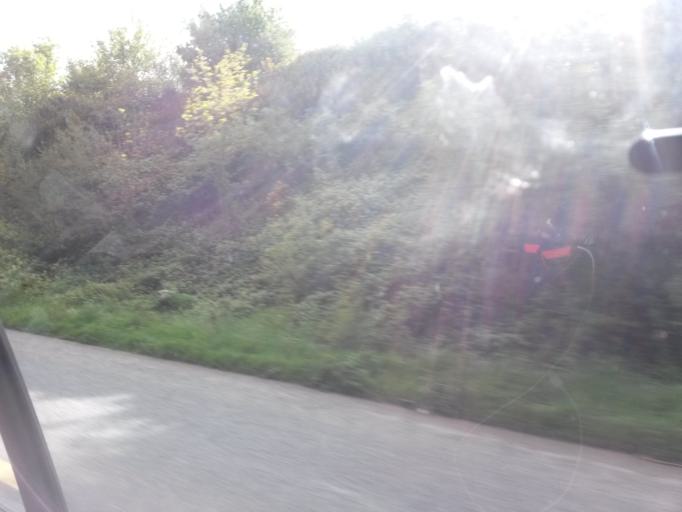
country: IE
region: Leinster
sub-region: Loch Garman
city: Enniscorthy
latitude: 52.5289
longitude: -6.5575
